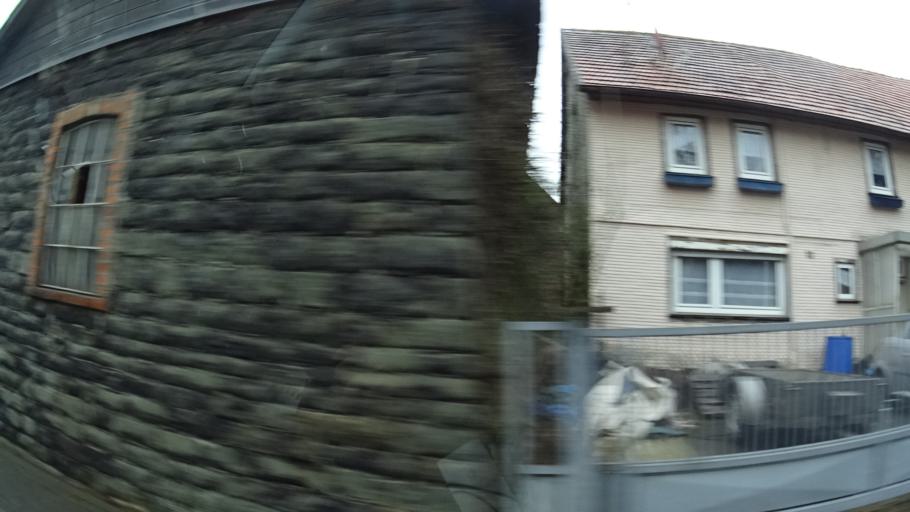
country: DE
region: Hesse
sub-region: Regierungsbezirk Giessen
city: Ulrichstein
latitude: 50.6054
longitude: 9.2264
